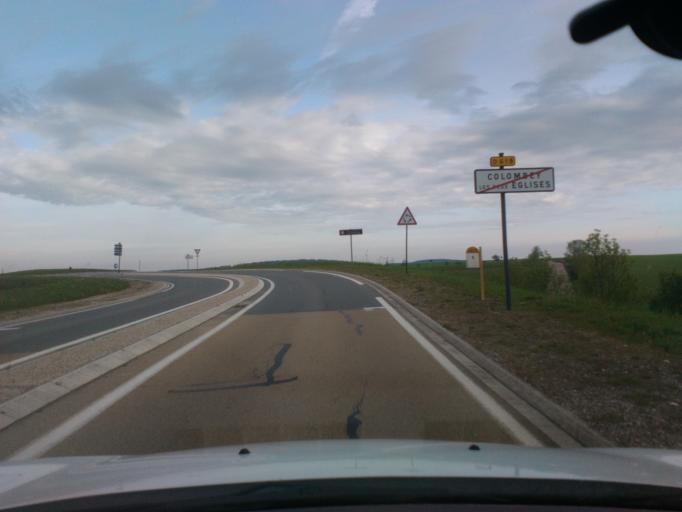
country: FR
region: Champagne-Ardenne
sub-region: Departement de la Haute-Marne
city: Lavilleneuve-au-Roi
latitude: 48.2269
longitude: 4.8847
